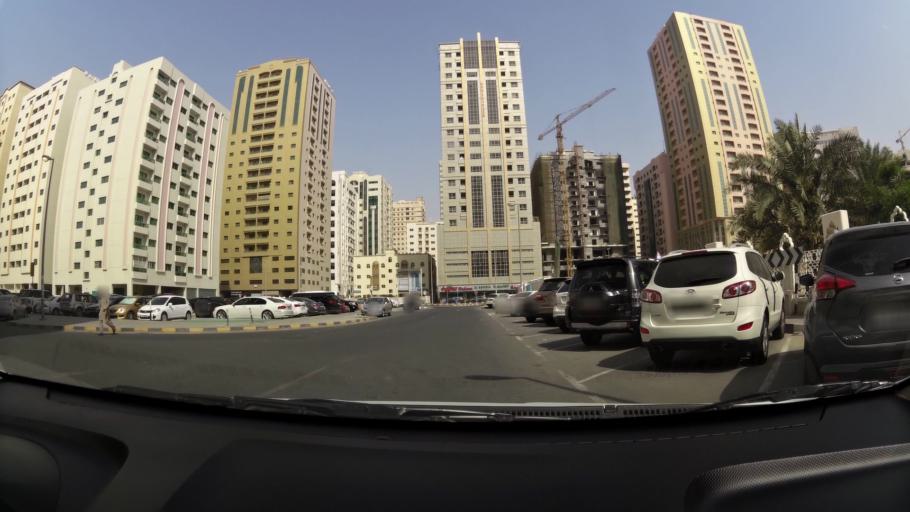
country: AE
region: Ash Shariqah
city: Sharjah
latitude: 25.3442
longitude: 55.3896
